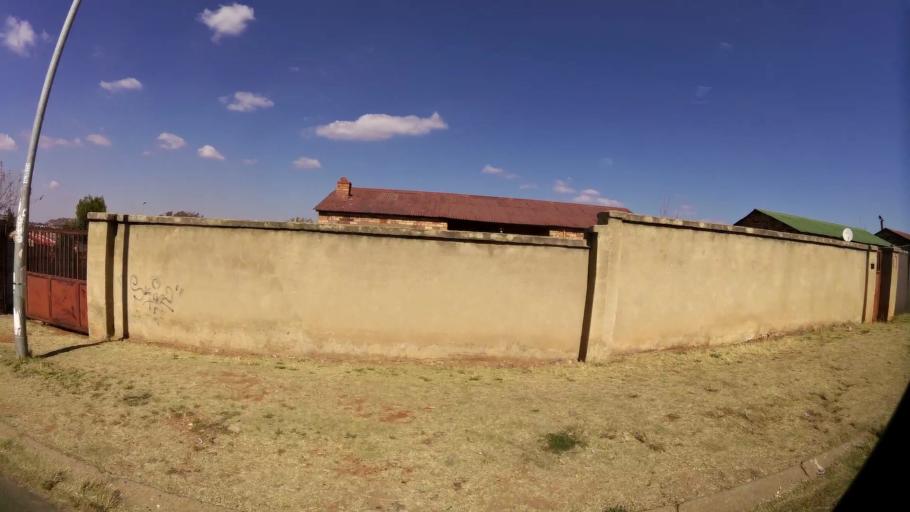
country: ZA
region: Gauteng
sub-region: City of Johannesburg Metropolitan Municipality
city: Soweto
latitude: -26.2408
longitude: 27.9060
